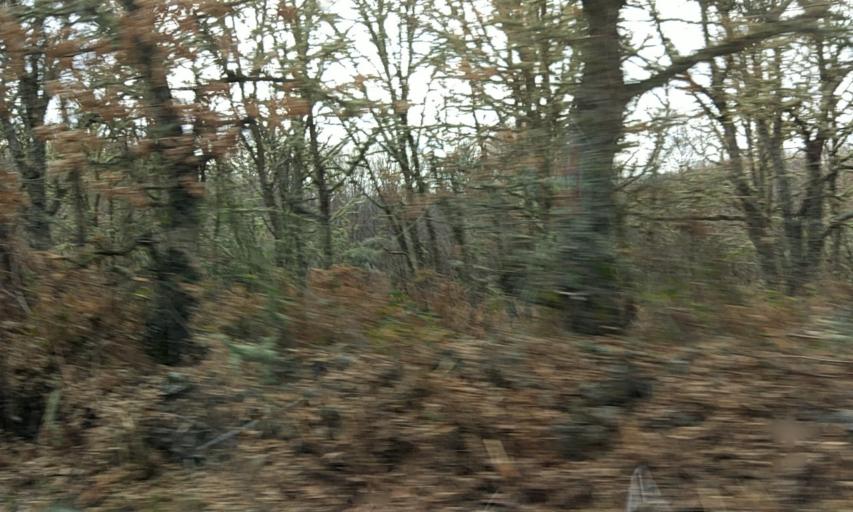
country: ES
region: Castille and Leon
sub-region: Provincia de Salamanca
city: Penaparda
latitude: 40.2954
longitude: -6.6611
